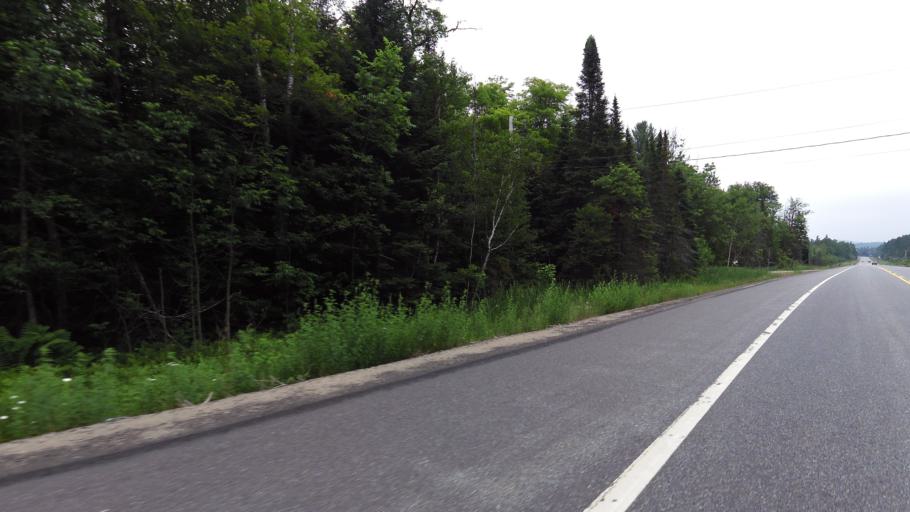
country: CA
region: Ontario
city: Huntsville
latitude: 45.3582
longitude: -78.9313
